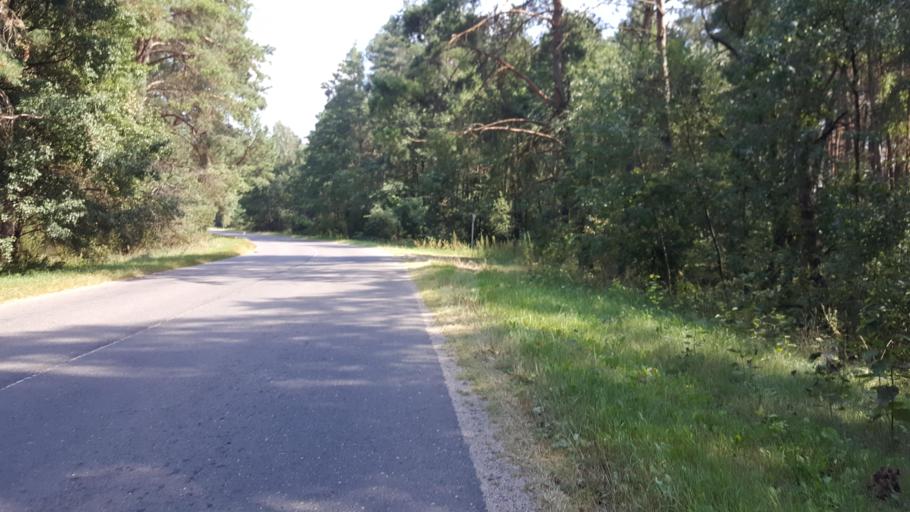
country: BY
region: Brest
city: Kamyanyuki
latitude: 52.5047
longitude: 23.6424
